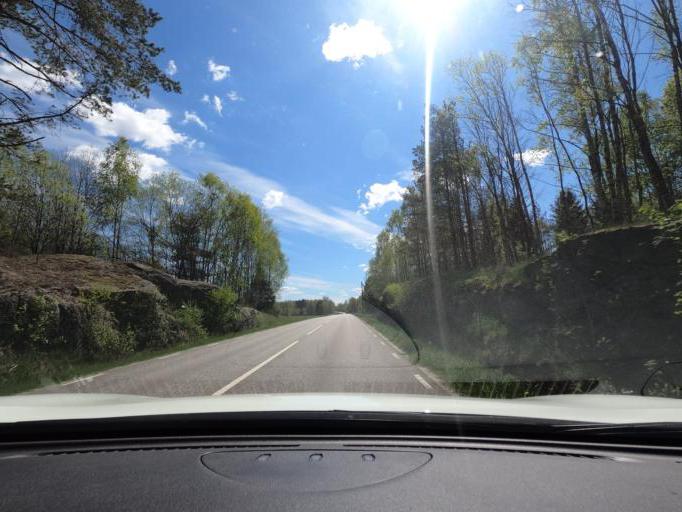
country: SE
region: Halland
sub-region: Kungsbacka Kommun
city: Fjaeras kyrkby
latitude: 57.4016
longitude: 12.2303
